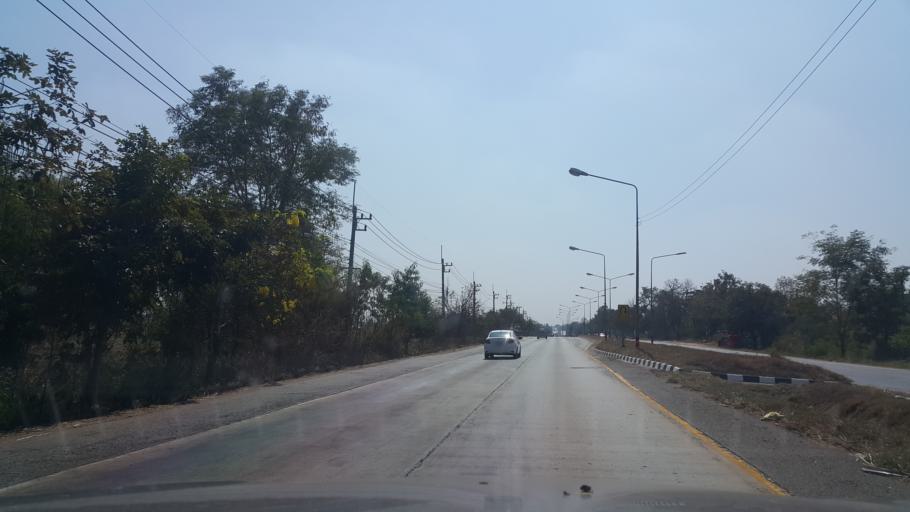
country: TH
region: Khon Kaen
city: Nam Phong
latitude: 16.8265
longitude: 102.8409
